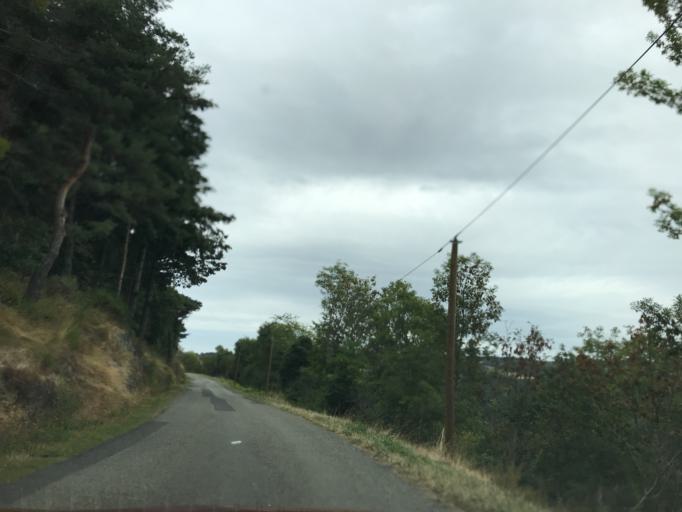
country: FR
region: Rhone-Alpes
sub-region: Departement de la Loire
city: Sail-sous-Couzan
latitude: 45.6926
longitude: 3.9198
